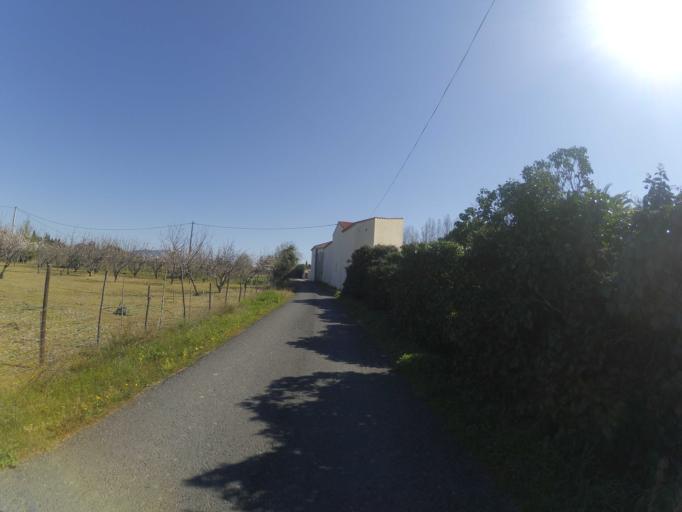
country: FR
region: Languedoc-Roussillon
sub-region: Departement des Pyrenees-Orientales
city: Ille-sur-Tet
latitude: 42.6620
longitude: 2.6267
